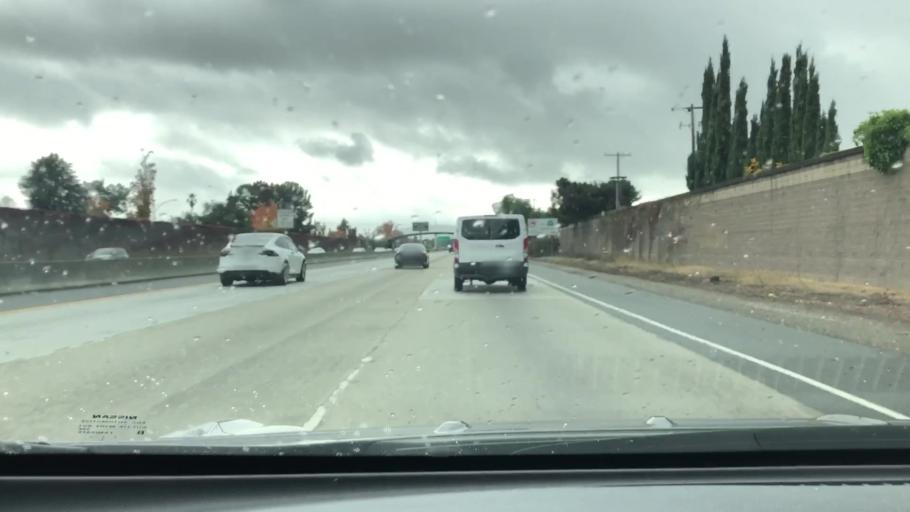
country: US
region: California
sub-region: Santa Clara County
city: Sunnyvale
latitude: 37.3482
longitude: -122.0601
